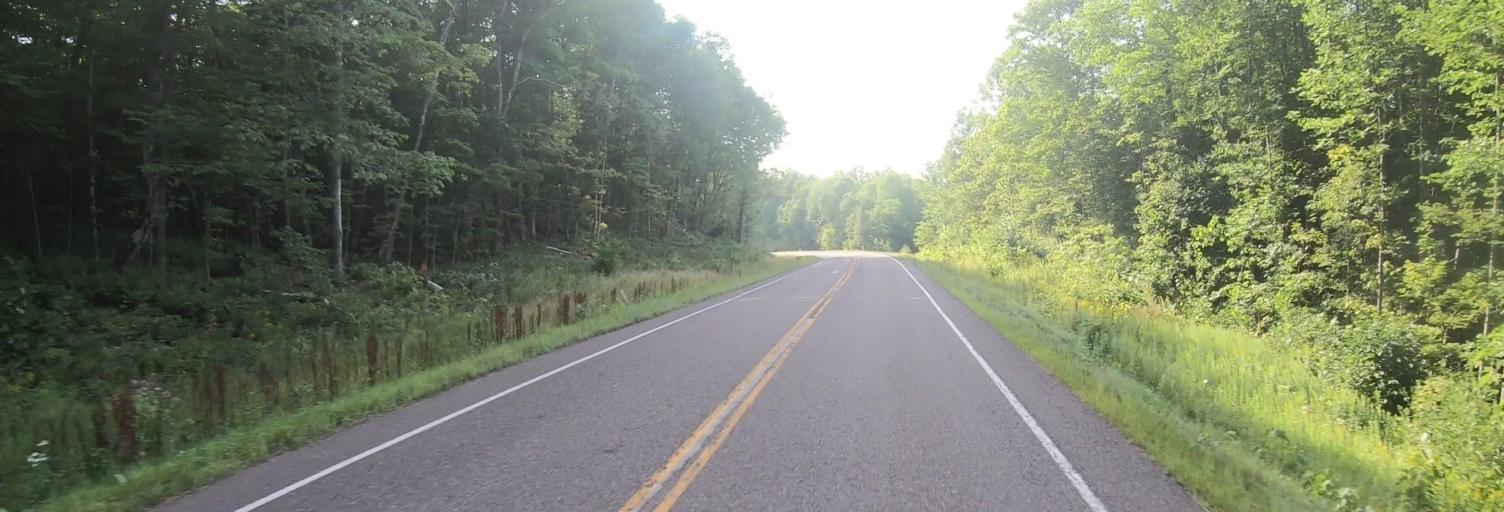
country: US
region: Wisconsin
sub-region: Ashland County
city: Ashland
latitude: 46.3102
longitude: -90.7408
